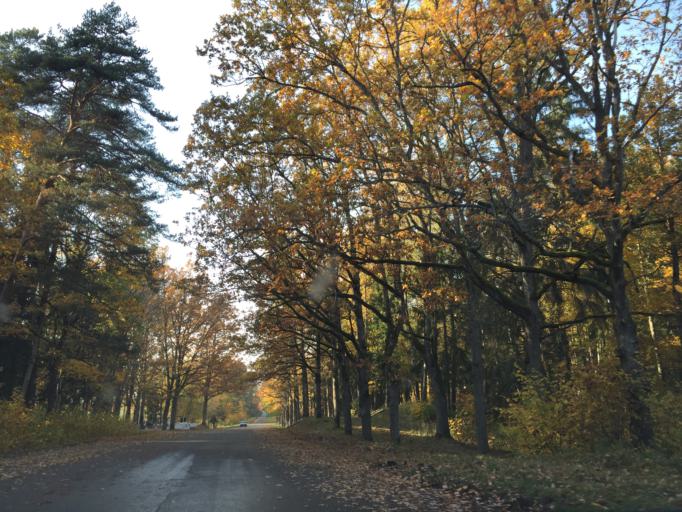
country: LV
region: Skrunda
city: Skrunda
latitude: 56.6777
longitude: 22.1581
